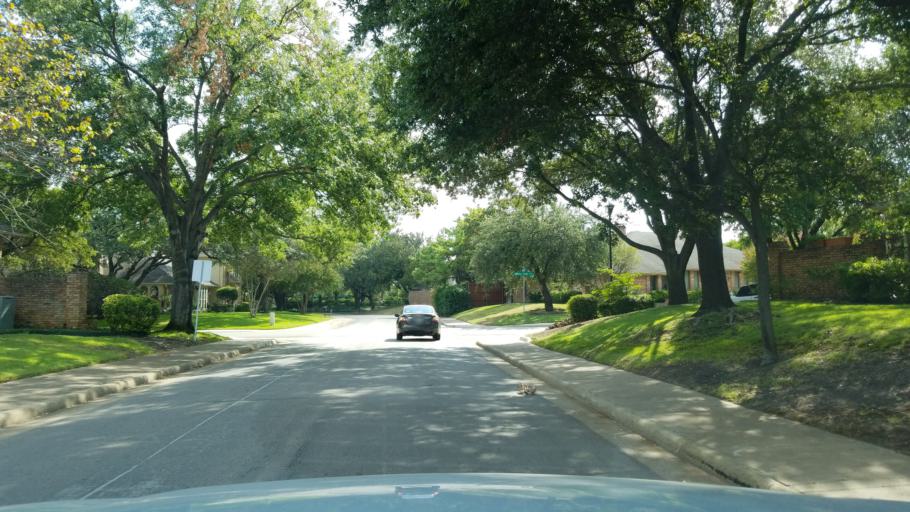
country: US
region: Texas
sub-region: Dallas County
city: Addison
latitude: 32.9641
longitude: -96.7980
